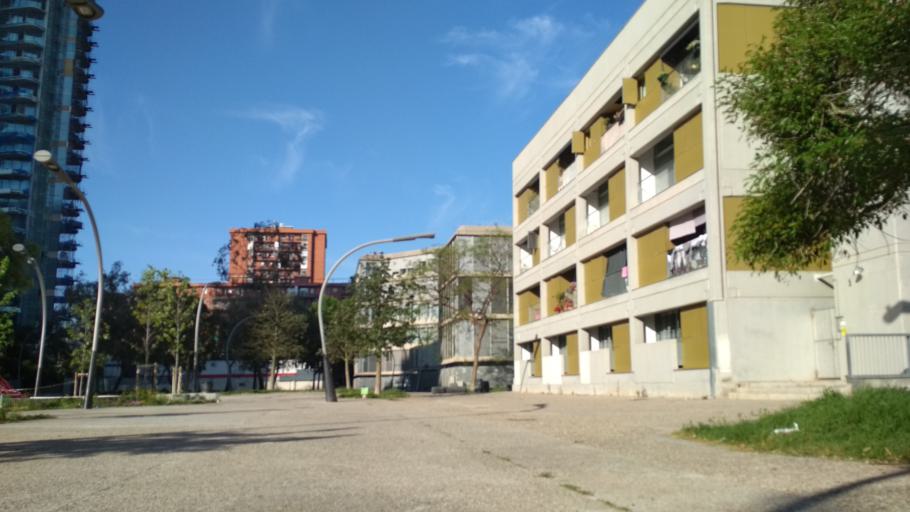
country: ES
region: Catalonia
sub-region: Provincia de Barcelona
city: Sant Adria de Besos
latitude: 41.4133
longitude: 2.2198
